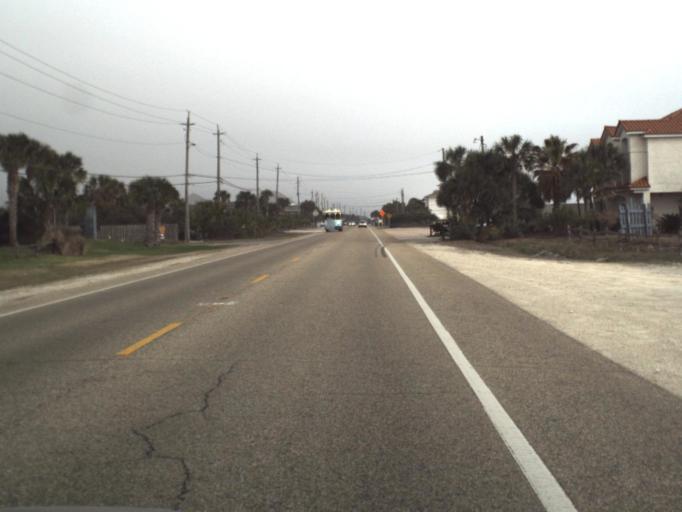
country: US
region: Florida
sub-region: Bay County
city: Laguna Beach
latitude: 30.2571
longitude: -85.9641
